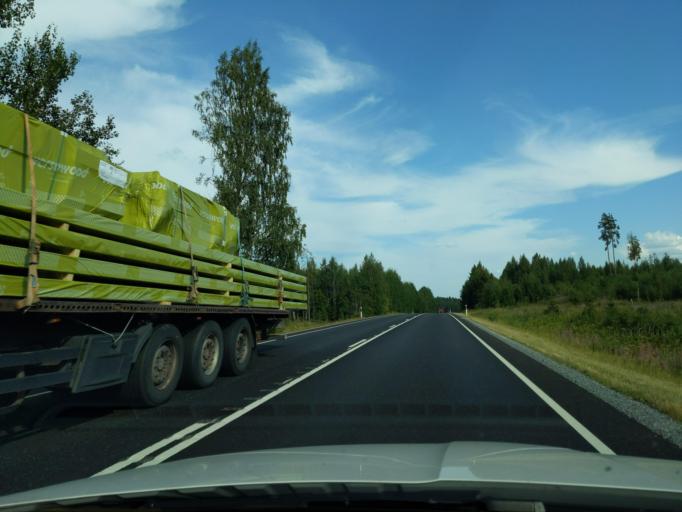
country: FI
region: Haeme
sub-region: Haemeenlinna
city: Tuulos
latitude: 61.1535
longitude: 24.7395
